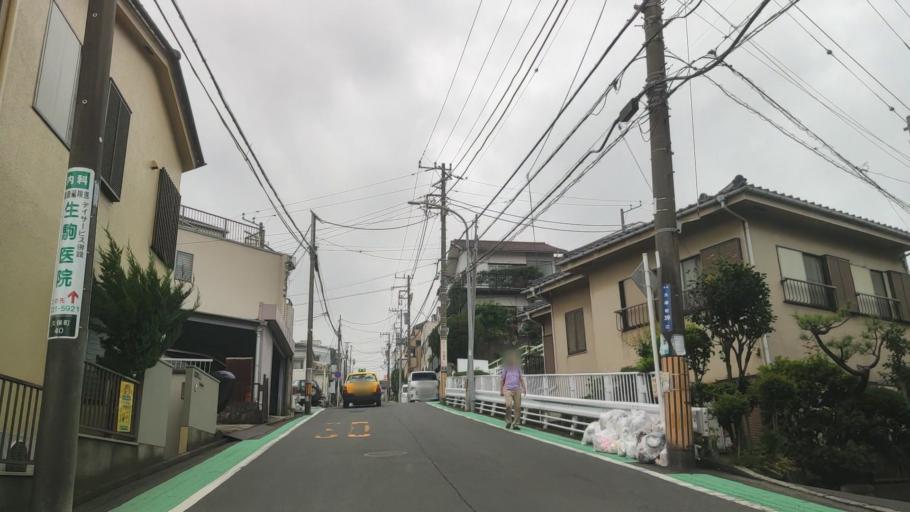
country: JP
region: Kanagawa
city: Yokohama
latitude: 35.4490
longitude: 139.6107
